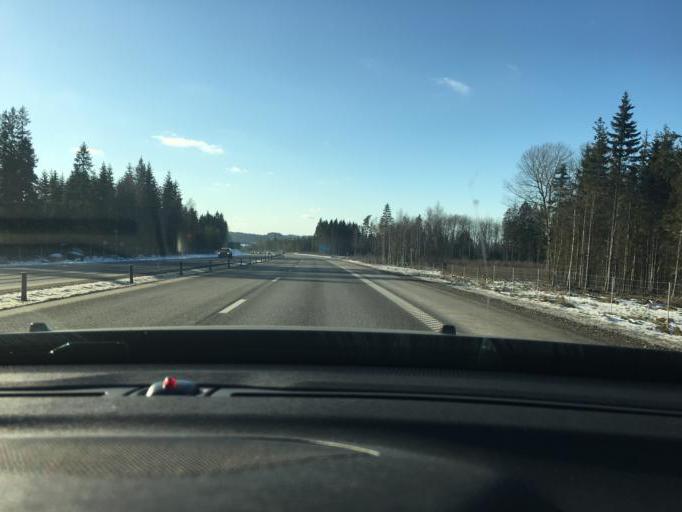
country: SE
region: Vaestra Goetaland
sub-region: Ulricehamns Kommun
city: Ulricehamn
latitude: 57.8213
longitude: 13.3180
